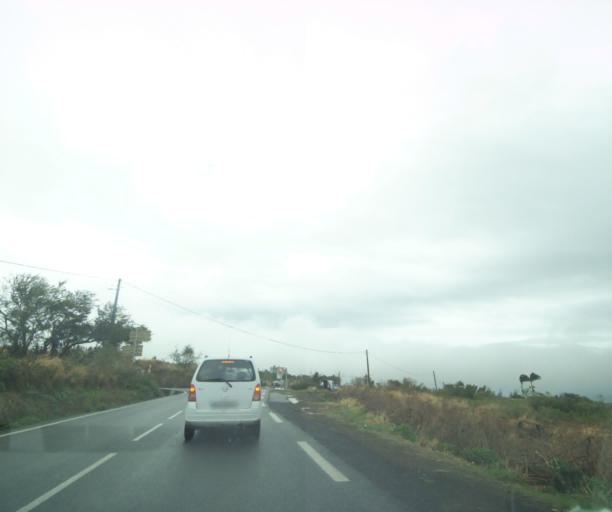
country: RE
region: Reunion
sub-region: Reunion
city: Saint-Paul
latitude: -21.0338
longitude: 55.2772
